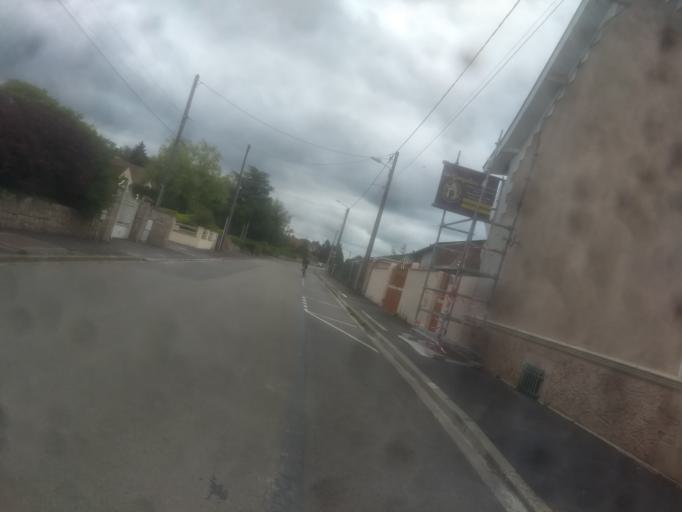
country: FR
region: Nord-Pas-de-Calais
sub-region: Departement du Pas-de-Calais
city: Saint-Nicolas
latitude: 50.3237
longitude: 2.7864
